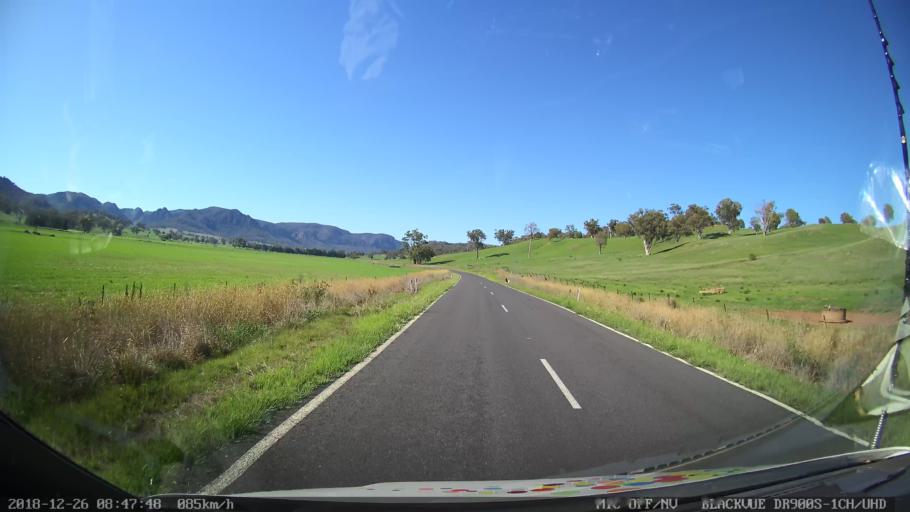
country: AU
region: New South Wales
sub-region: Mid-Western Regional
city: Kandos
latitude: -32.5469
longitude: 150.0893
